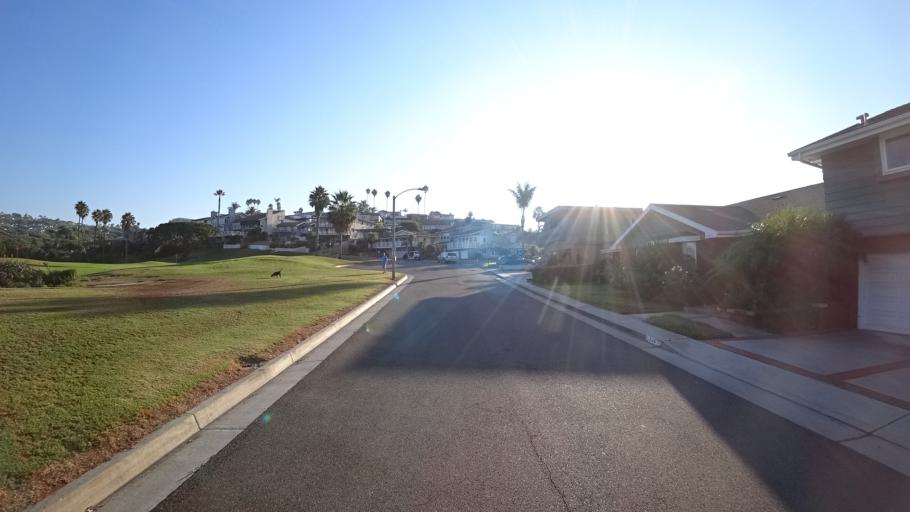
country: US
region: California
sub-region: Orange County
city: San Clemente
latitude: 33.4108
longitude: -117.5965
